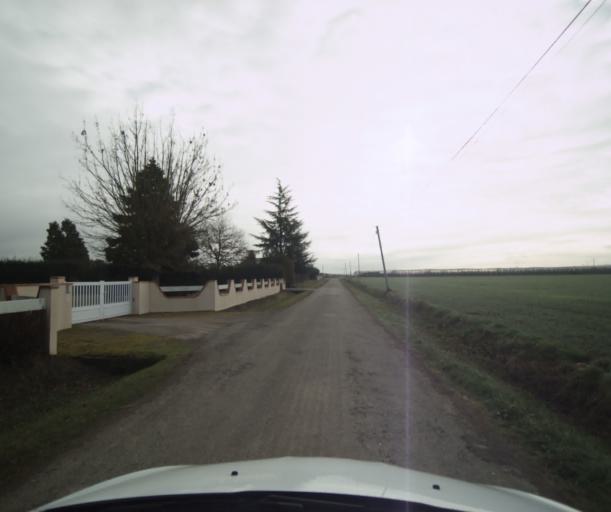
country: FR
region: Midi-Pyrenees
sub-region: Departement du Tarn-et-Garonne
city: Castelsarrasin
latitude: 44.0279
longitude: 1.1186
